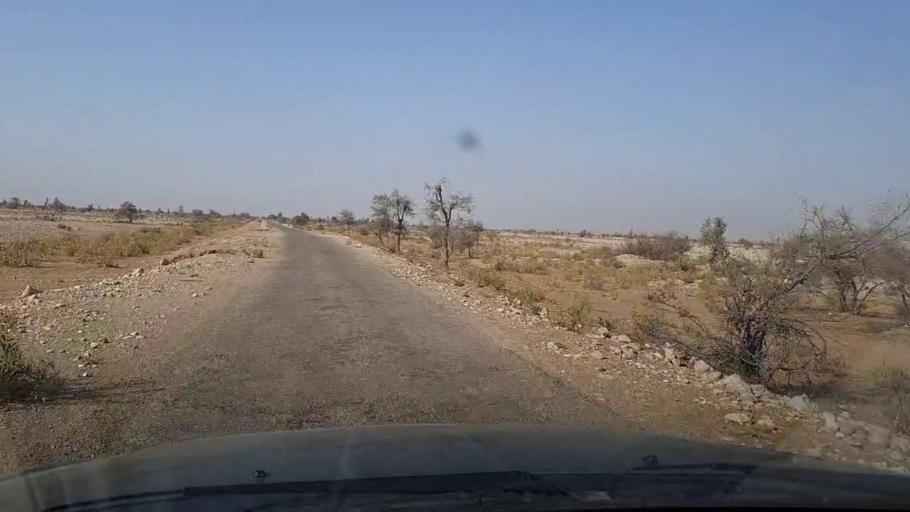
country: PK
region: Sindh
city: Sann
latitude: 25.9298
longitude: 68.0208
